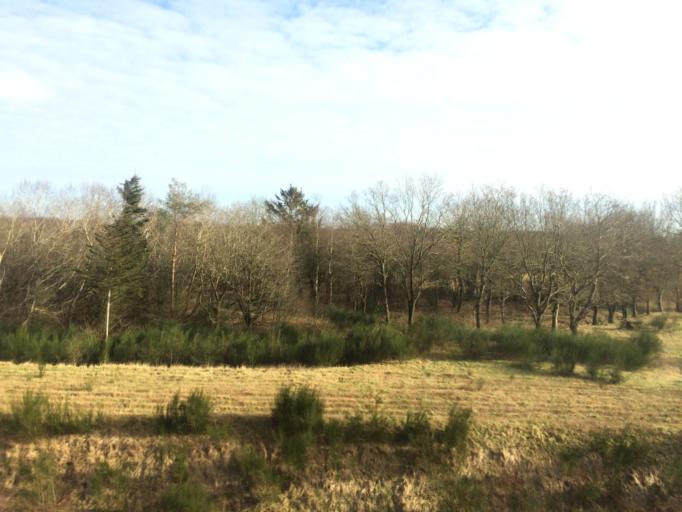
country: DK
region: South Denmark
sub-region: Vejle Kommune
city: Give
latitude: 55.8749
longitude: 9.2408
